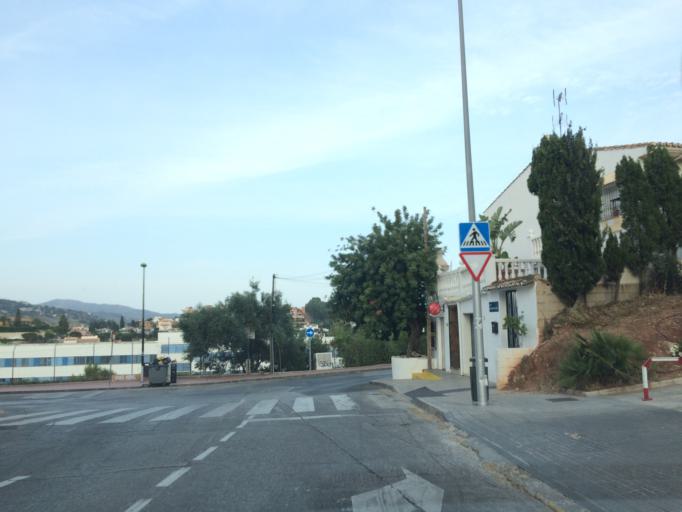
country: ES
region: Andalusia
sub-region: Provincia de Malaga
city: Malaga
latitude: 36.7271
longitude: -4.3859
